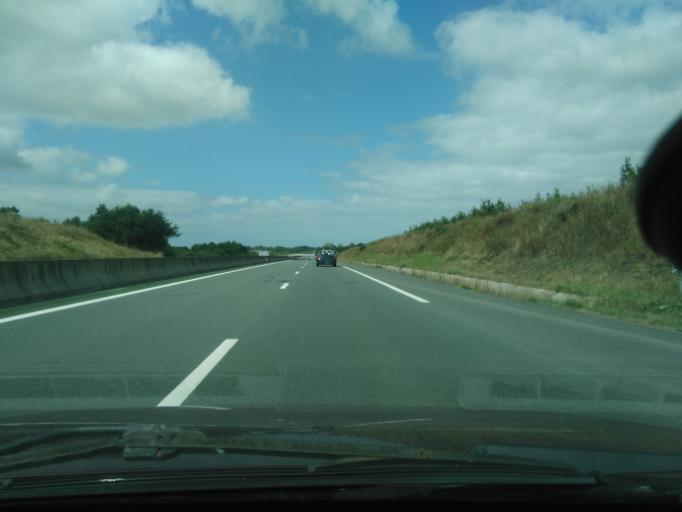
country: FR
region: Pays de la Loire
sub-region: Departement de la Vendee
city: Aubigny
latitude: 46.6295
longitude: -1.4503
